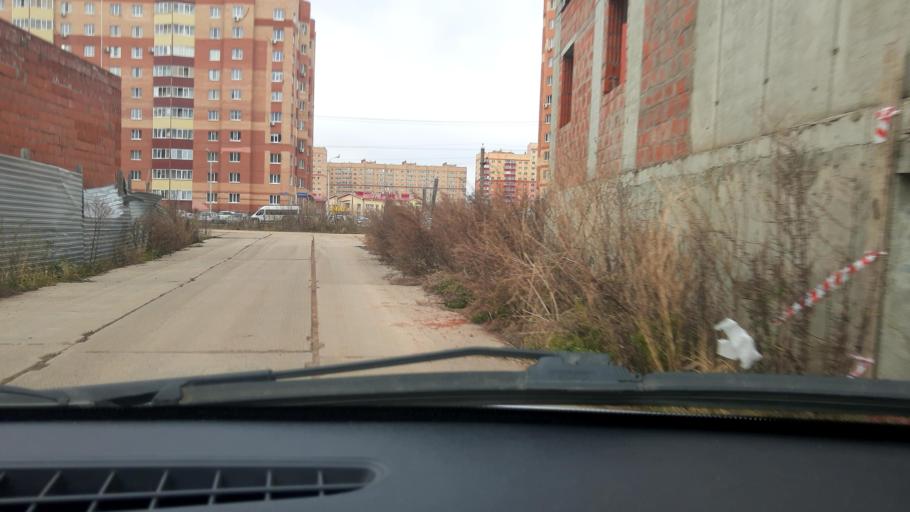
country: RU
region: Bashkortostan
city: Mikhaylovka
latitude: 54.7130
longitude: 55.8451
